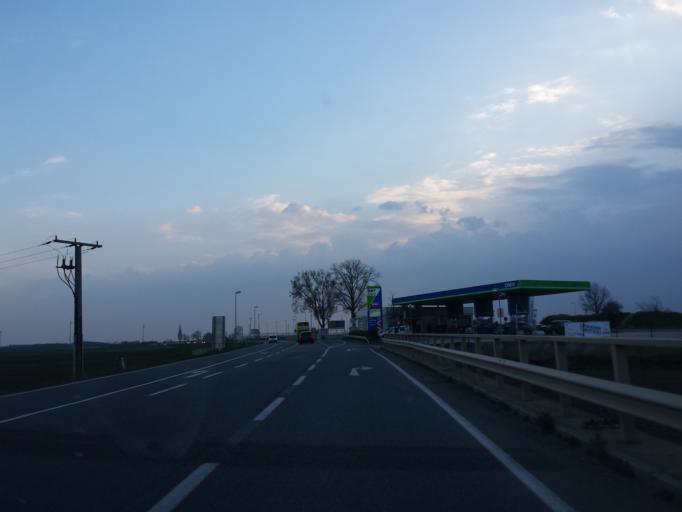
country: AT
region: Lower Austria
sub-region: Politischer Bezirk Mistelbach
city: Wilfersdorf
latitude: 48.5733
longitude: 16.6400
